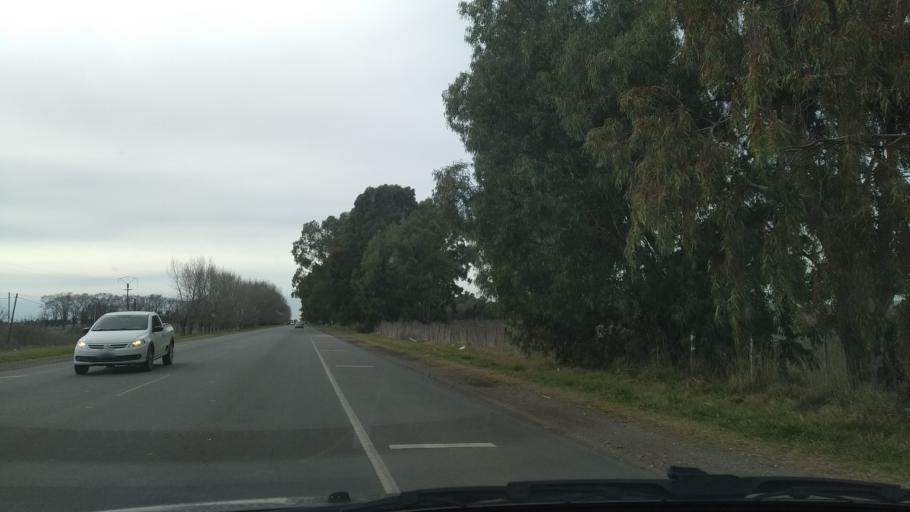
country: AR
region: Buenos Aires
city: Olavarria
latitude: -36.9710
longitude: -60.2734
